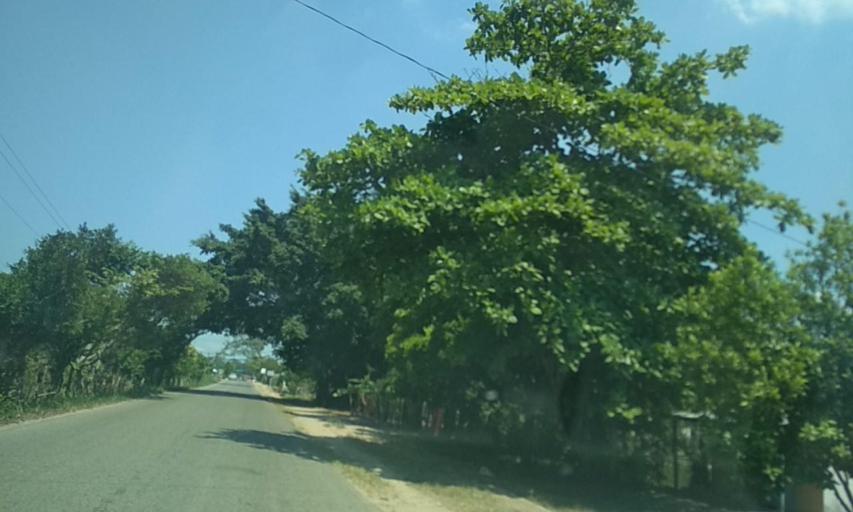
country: MX
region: Tabasco
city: Huimanguillo
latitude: 17.7930
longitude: -93.4431
